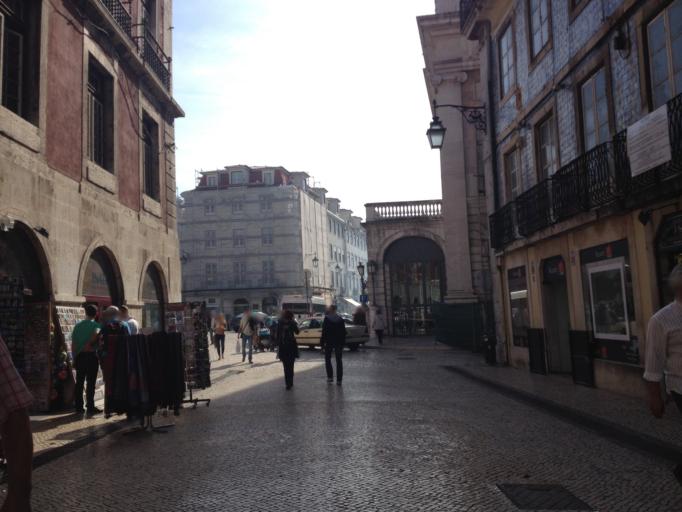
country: PT
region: Lisbon
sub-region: Lisbon
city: Lisbon
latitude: 38.7153
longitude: -9.1395
